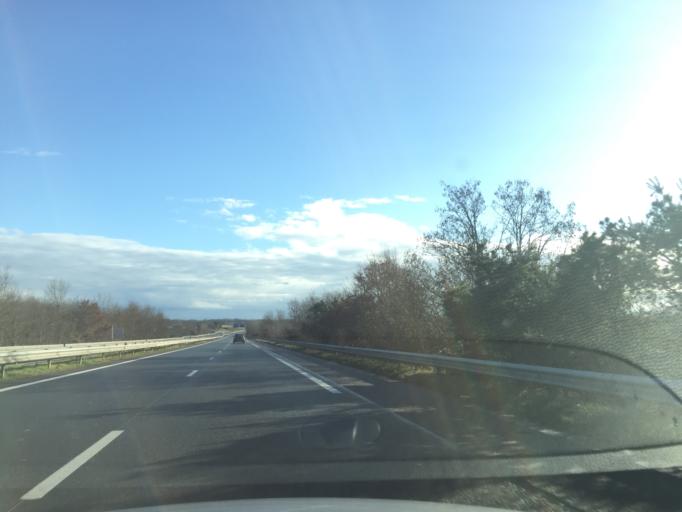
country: FR
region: Rhone-Alpes
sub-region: Departement de la Loire
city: Balbigny
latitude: 45.8293
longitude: 4.1029
